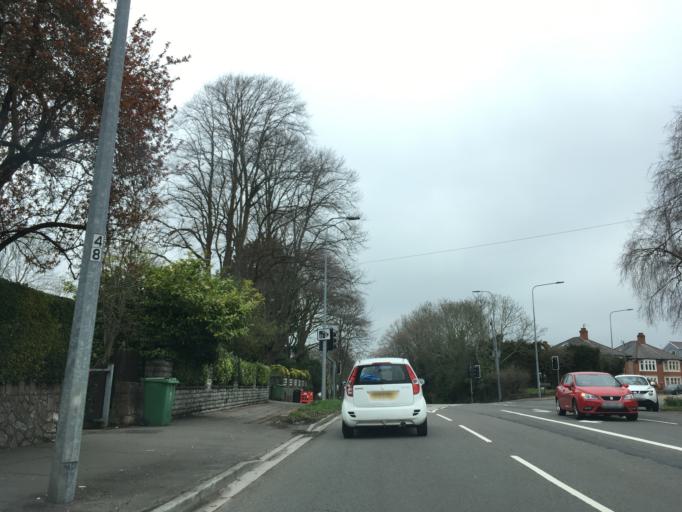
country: GB
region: Wales
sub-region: Cardiff
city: Cardiff
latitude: 51.5169
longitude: -3.1859
